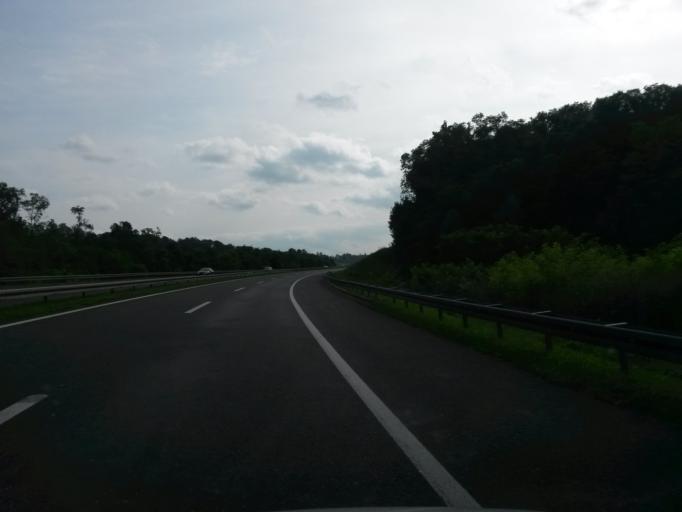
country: HR
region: Varazdinska
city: Jalzabet
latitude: 46.2371
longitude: 16.4107
